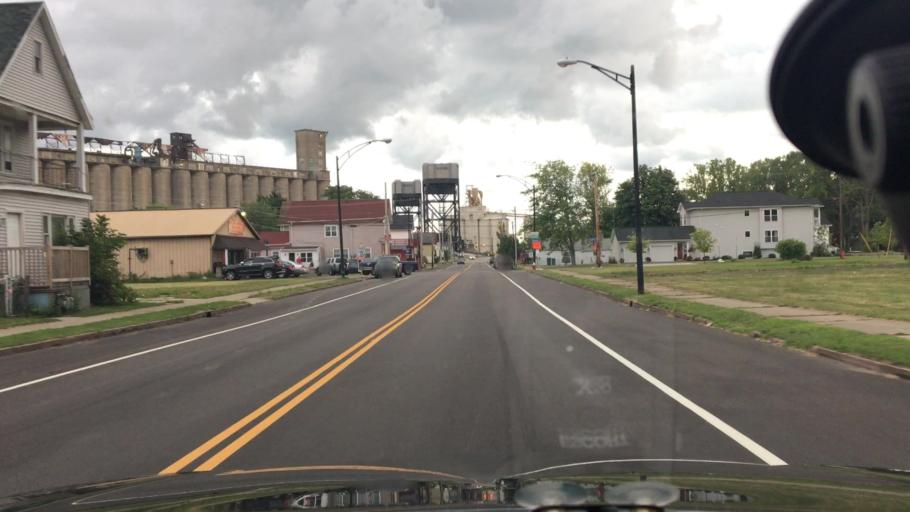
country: US
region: New York
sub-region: Erie County
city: Buffalo
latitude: 42.8660
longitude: -78.8664
